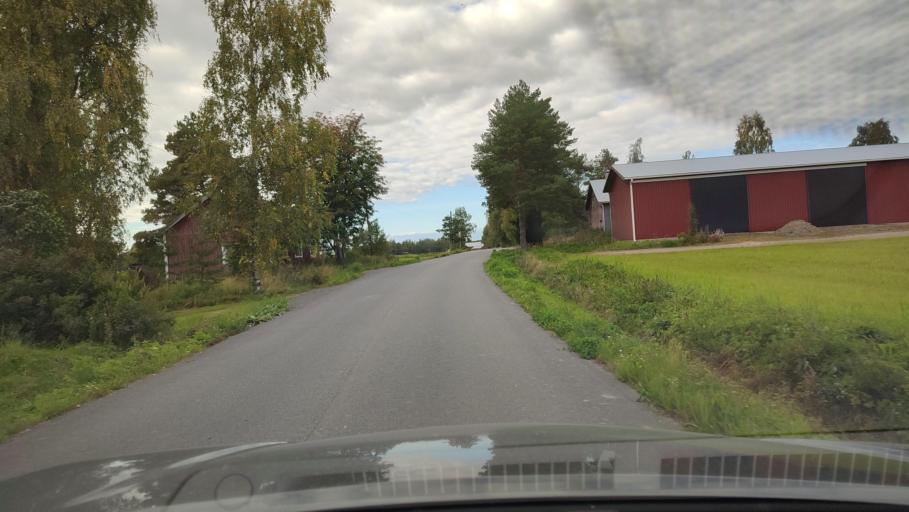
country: FI
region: Southern Ostrobothnia
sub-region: Suupohja
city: Karijoki
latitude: 62.2372
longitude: 21.5913
